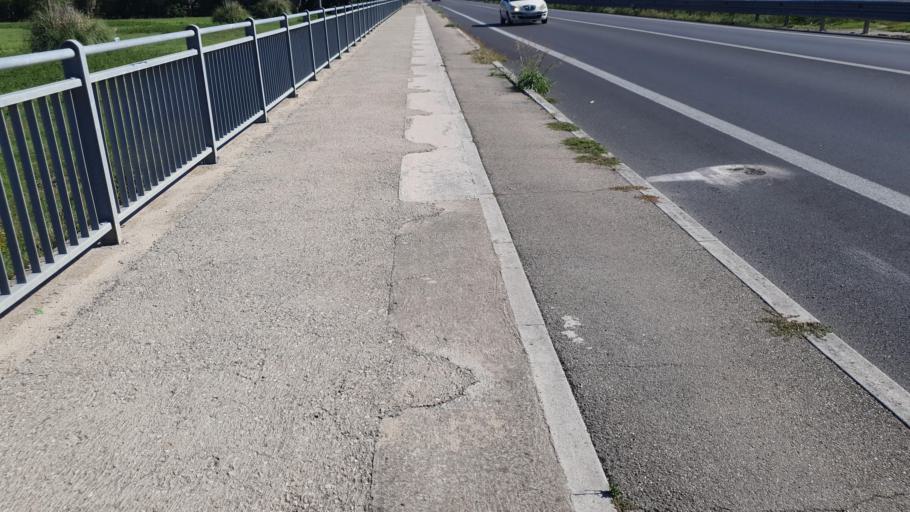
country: IT
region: Abruzzo
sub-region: Provincia di Chieti
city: Salvo Marina
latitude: 42.0654
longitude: 14.7784
